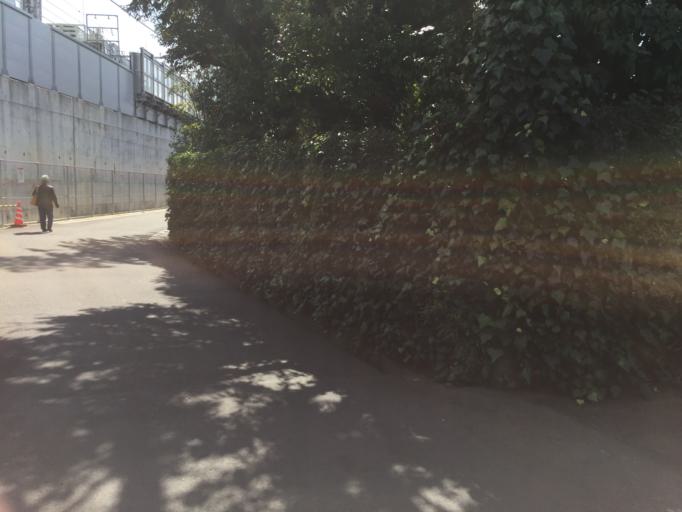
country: JP
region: Tokyo
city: Tokyo
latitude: 35.6386
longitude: 139.6917
